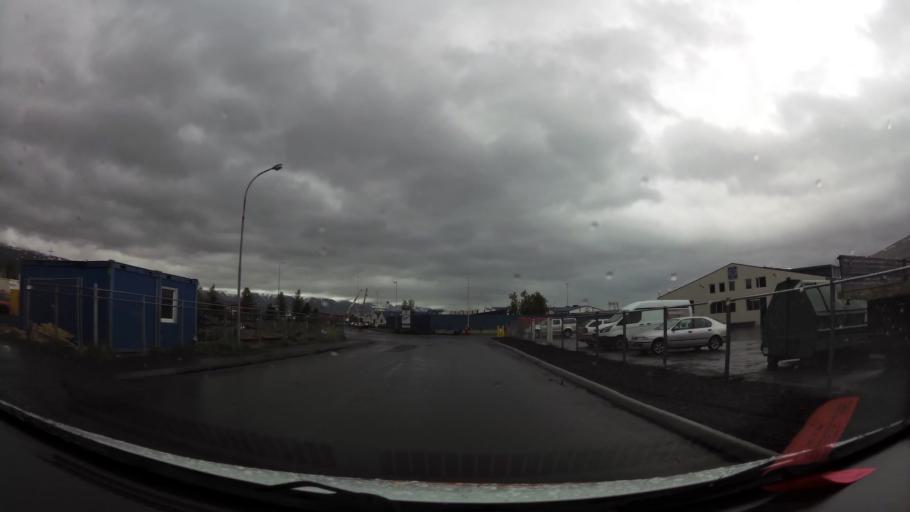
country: IS
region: Northeast
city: Akureyri
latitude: 65.6887
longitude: -18.0823
